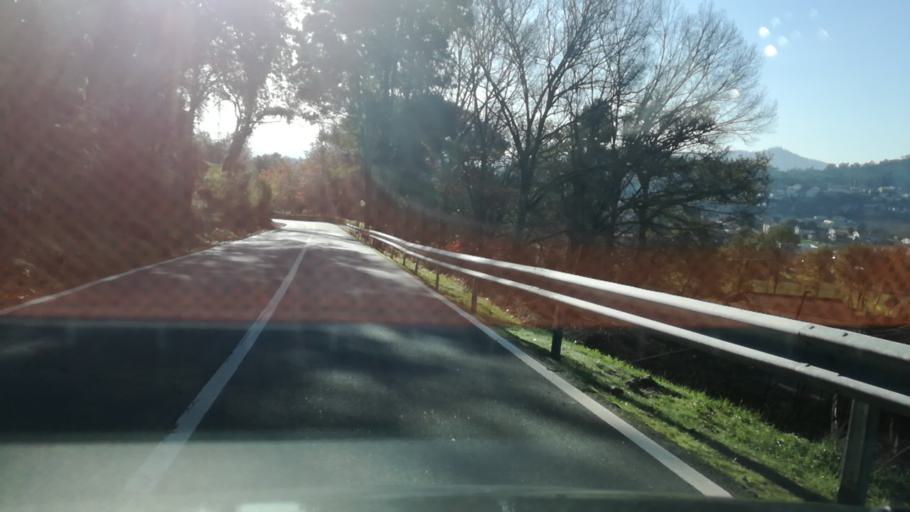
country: PT
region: Braga
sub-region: Guimaraes
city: Ponte
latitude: 41.5249
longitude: -8.3216
